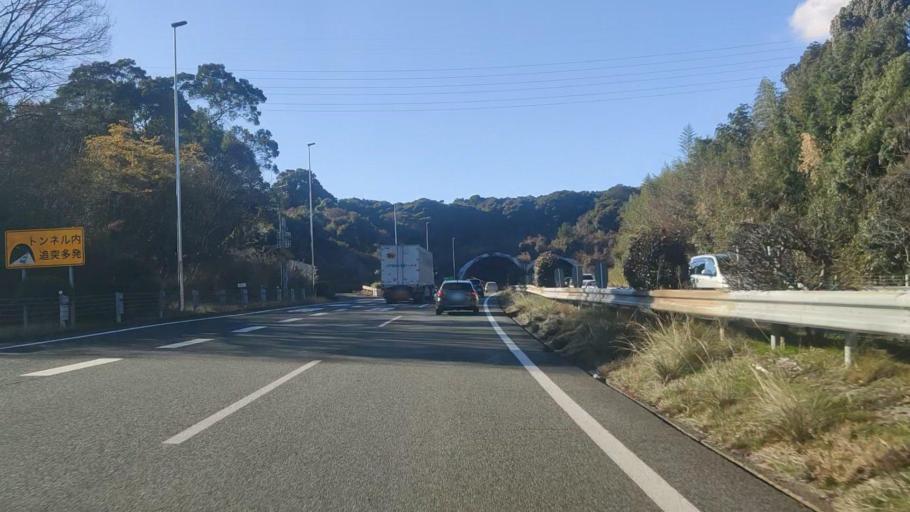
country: JP
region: Fukuoka
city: Miyata
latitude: 33.7563
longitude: 130.6565
